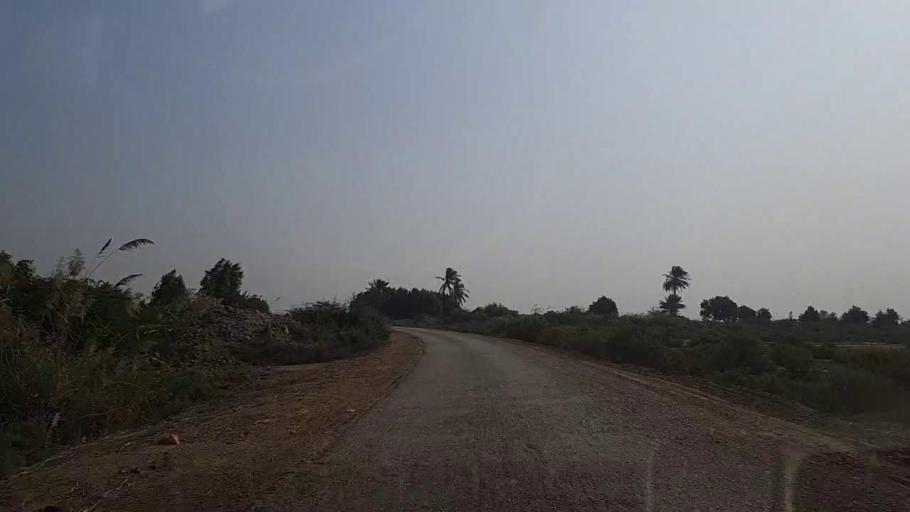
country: PK
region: Sindh
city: Keti Bandar
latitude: 24.2361
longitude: 67.6408
